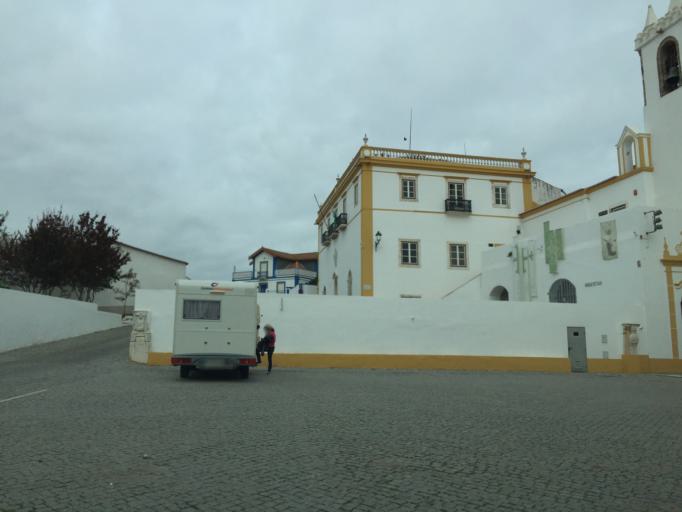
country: PT
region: Portalegre
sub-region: Avis
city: Avis
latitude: 39.0560
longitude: -7.8895
